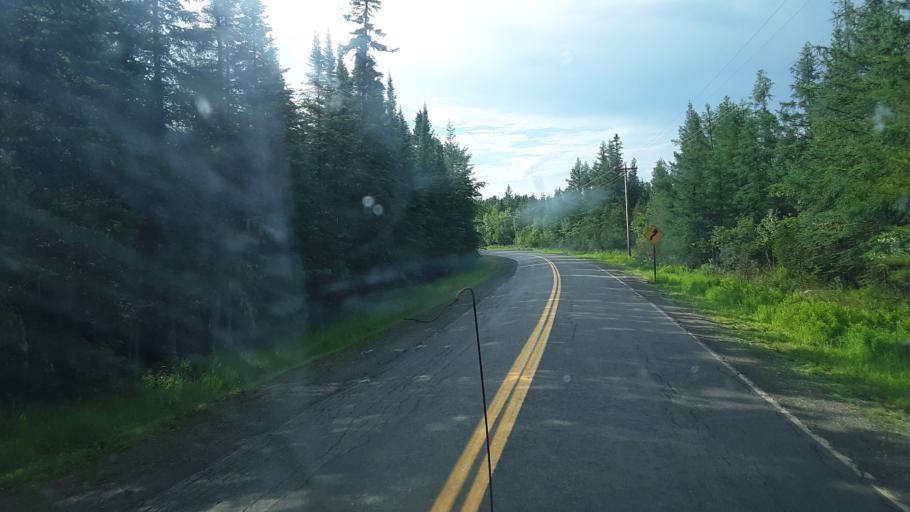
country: US
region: Maine
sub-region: Washington County
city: Calais
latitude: 45.1891
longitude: -67.5198
